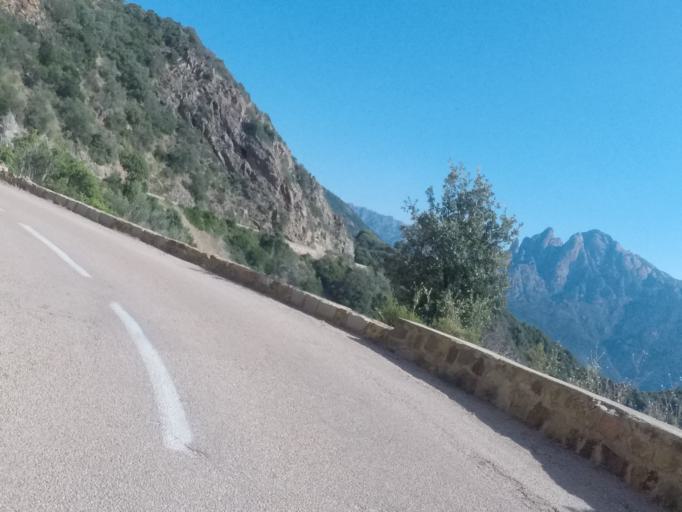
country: FR
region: Corsica
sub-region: Departement de la Corse-du-Sud
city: Cargese
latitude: 42.2909
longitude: 8.6791
